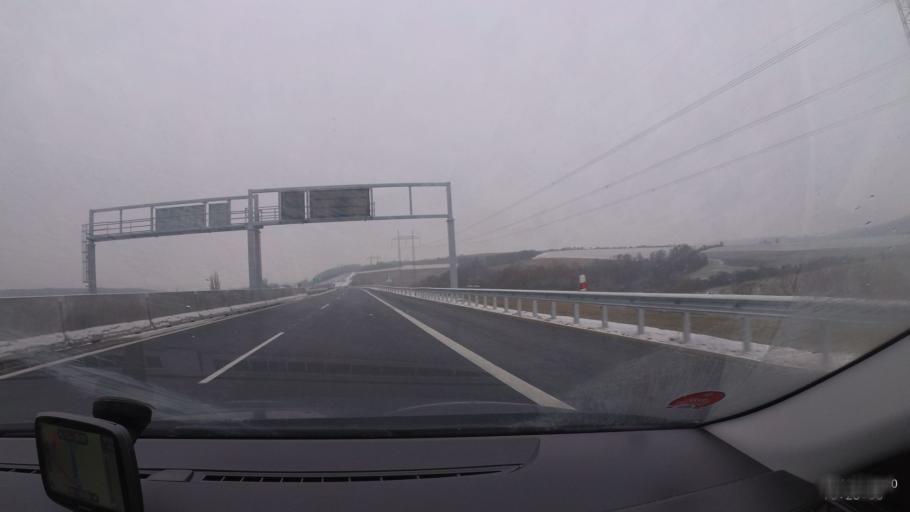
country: CZ
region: Central Bohemia
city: Revnicov
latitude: 50.1777
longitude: 13.7842
